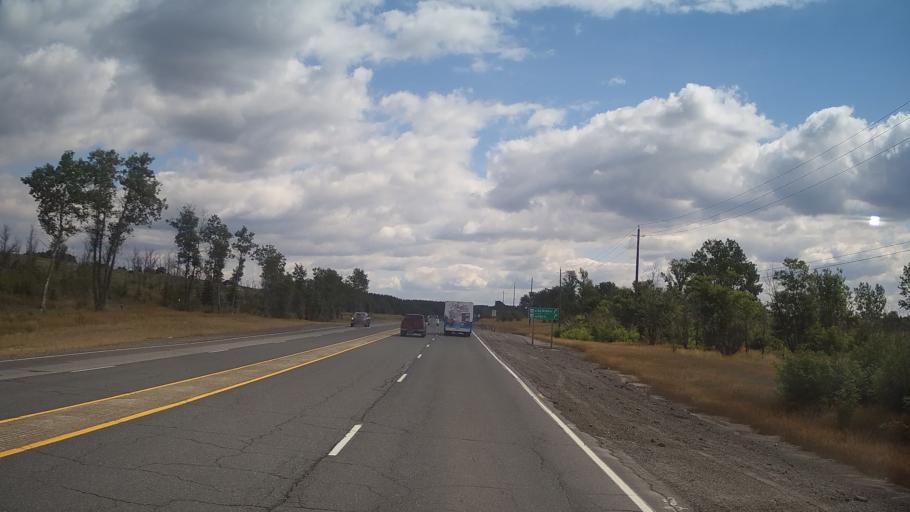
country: CA
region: Ontario
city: Greater Sudbury
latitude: 46.4705
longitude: -81.0508
